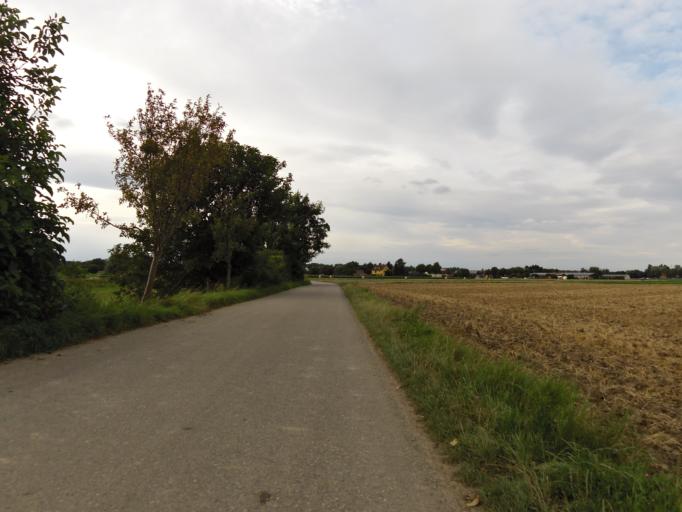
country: DE
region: Rheinland-Pfalz
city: Worms
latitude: 49.6291
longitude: 8.4025
